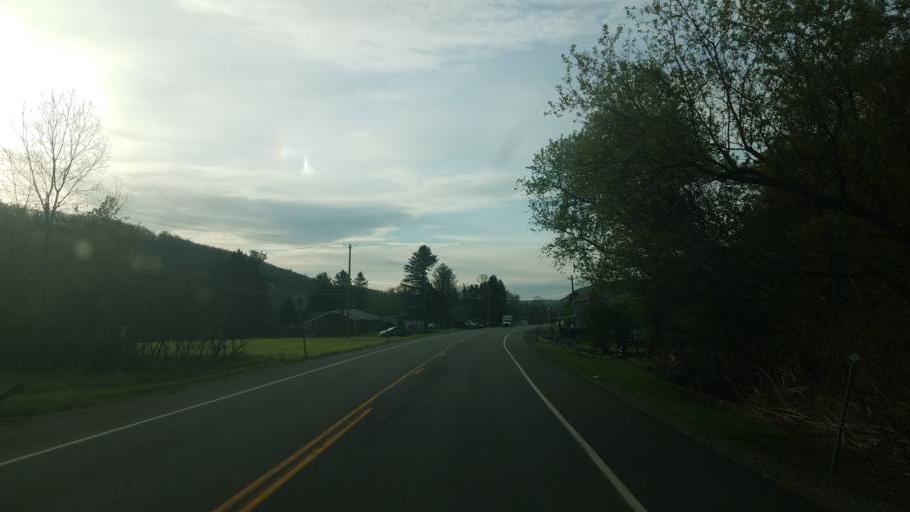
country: US
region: New York
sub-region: Steuben County
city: Hornell
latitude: 42.3430
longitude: -77.6985
